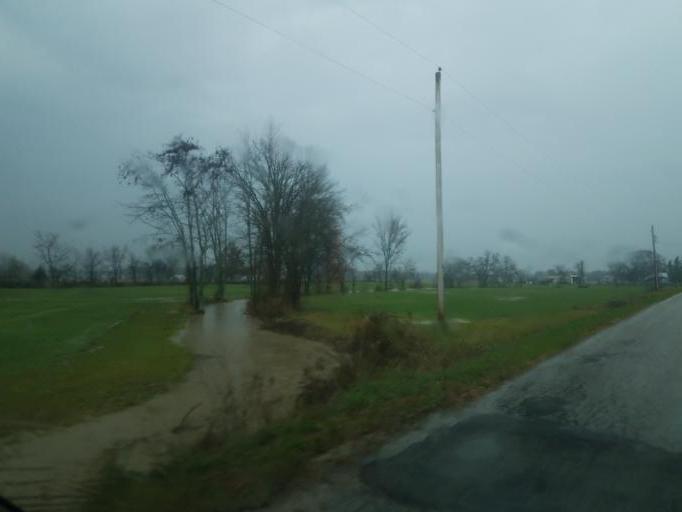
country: US
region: Ohio
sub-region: Morrow County
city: Cardington
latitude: 40.4551
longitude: -82.8714
